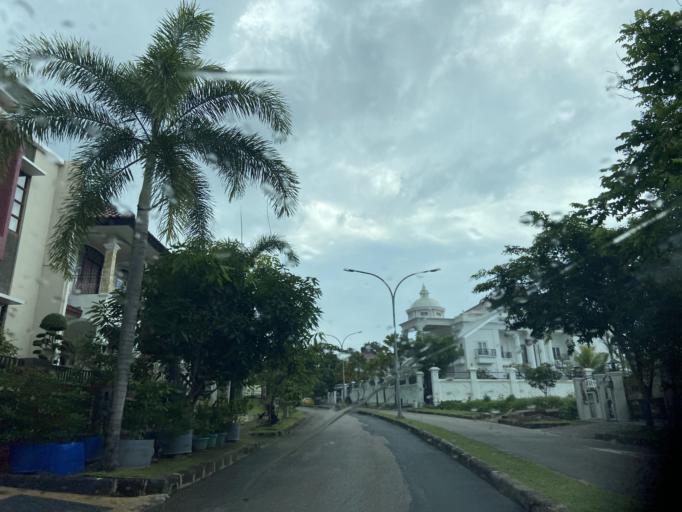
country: SG
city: Singapore
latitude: 1.1060
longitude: 104.0253
